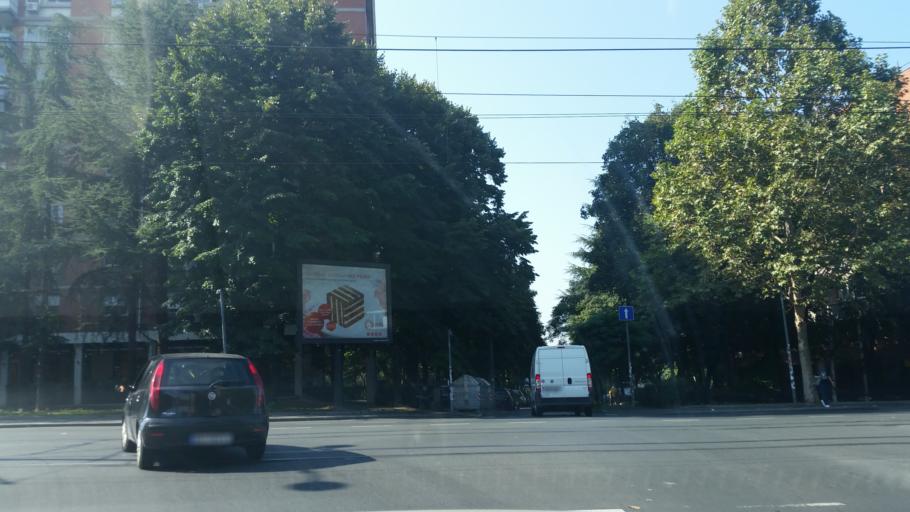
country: RS
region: Central Serbia
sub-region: Belgrade
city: Palilula
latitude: 44.7956
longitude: 20.4991
